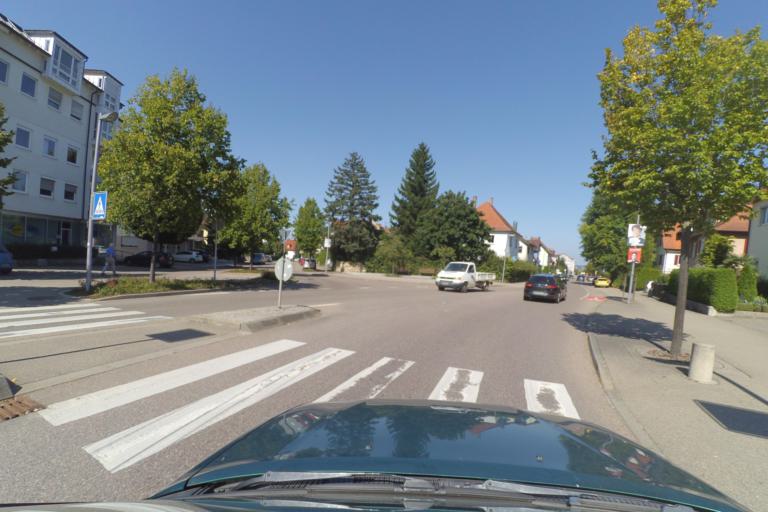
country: DE
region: Baden-Wuerttemberg
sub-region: Regierungsbezirk Stuttgart
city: Heubach
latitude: 48.7928
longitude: 9.9343
